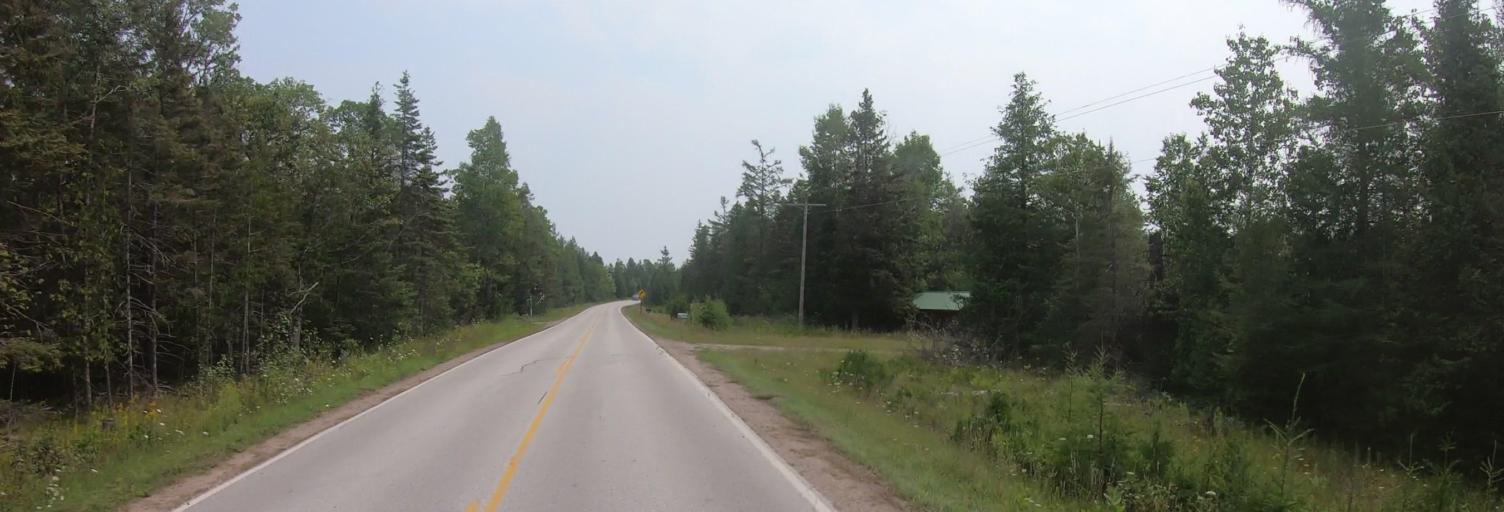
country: CA
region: Ontario
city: Thessalon
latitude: 45.9841
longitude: -83.6811
